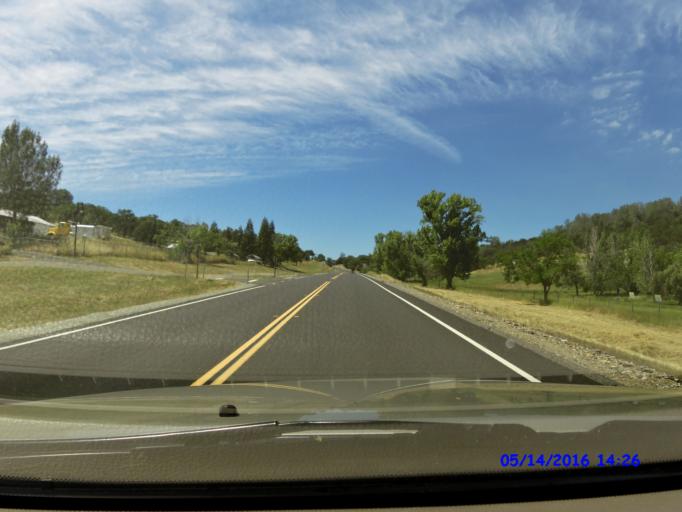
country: US
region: California
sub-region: Tuolumne County
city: Tuolumne City
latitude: 37.7126
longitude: -120.1990
